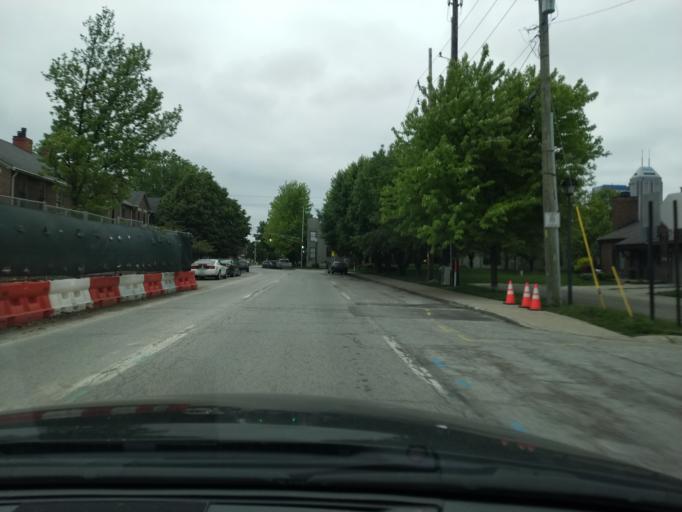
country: US
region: Indiana
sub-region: Marion County
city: Indianapolis
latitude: 39.7785
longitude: -86.1488
